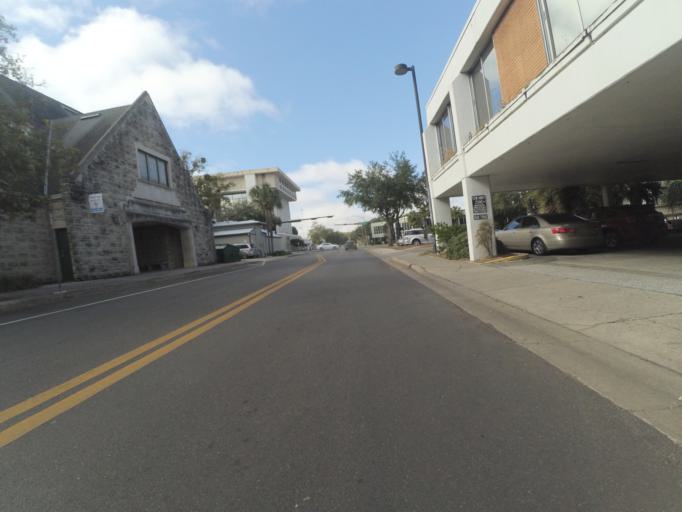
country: US
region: Florida
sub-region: Alachua County
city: Gainesville
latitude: 29.6535
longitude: -82.3241
